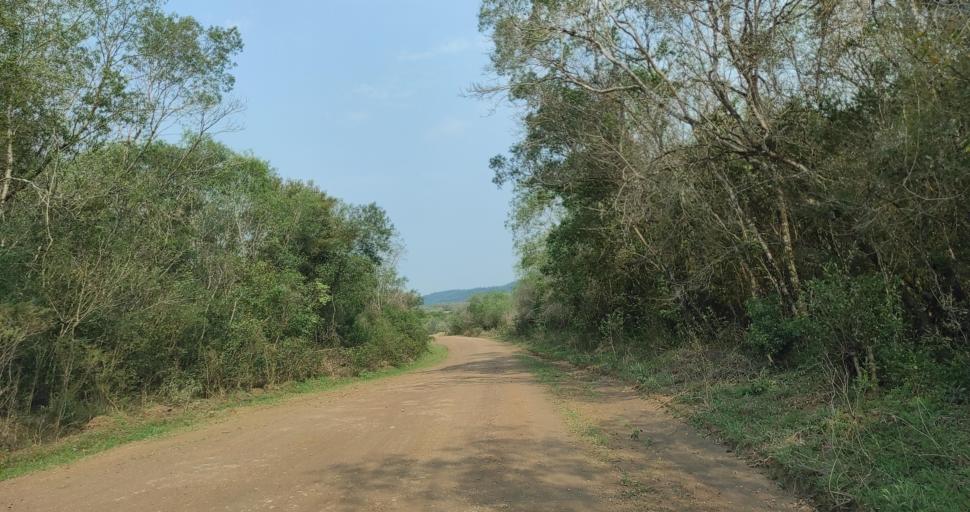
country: AR
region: Misiones
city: Cerro Cora
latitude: -27.5893
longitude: -55.5797
